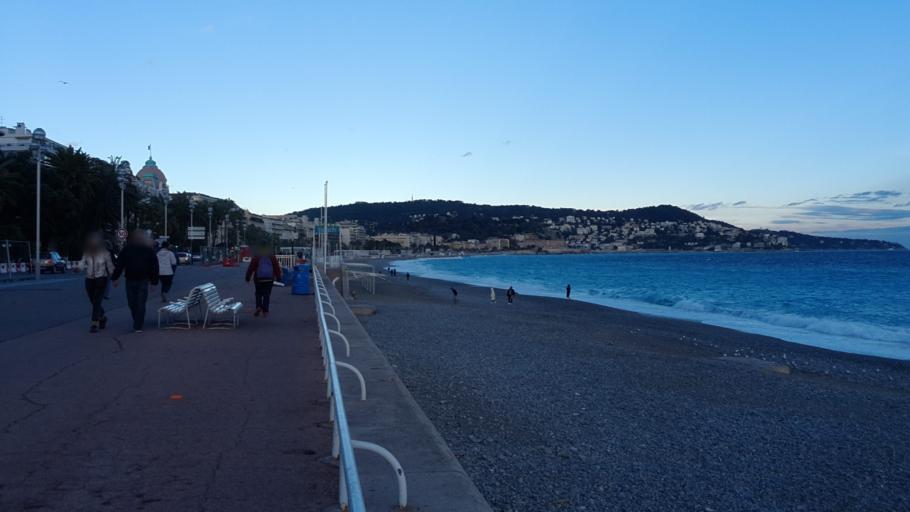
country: FR
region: Provence-Alpes-Cote d'Azur
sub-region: Departement des Alpes-Maritimes
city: Nice
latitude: 43.6932
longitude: 7.2544
